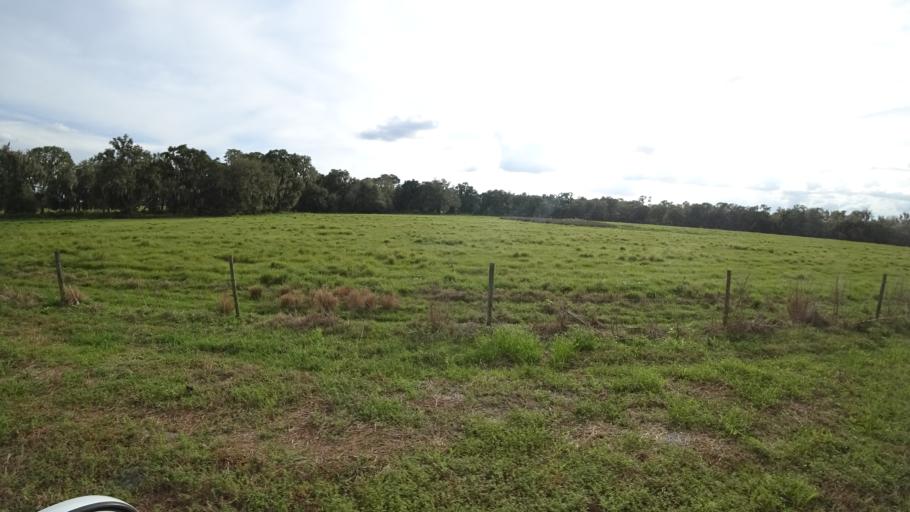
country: US
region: Florida
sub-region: Hillsborough County
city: Wimauma
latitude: 27.5526
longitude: -82.0939
